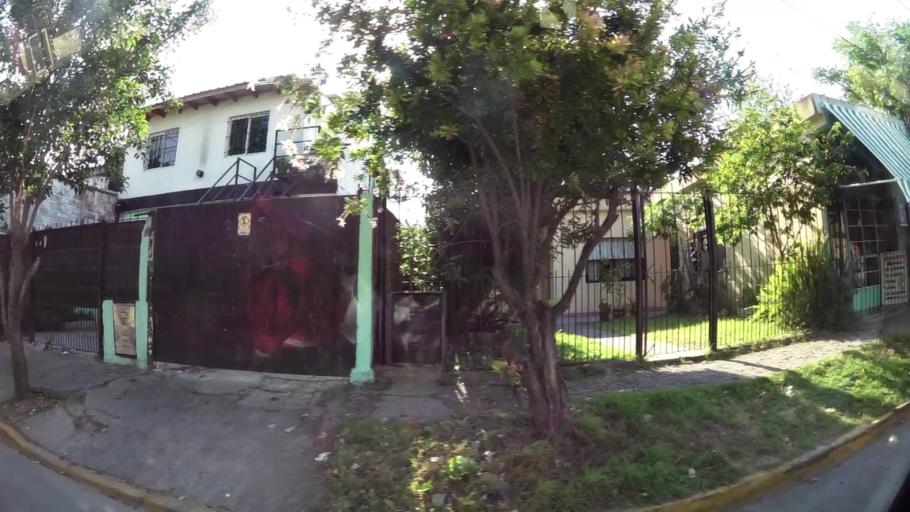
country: AR
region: Buenos Aires
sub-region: Partido de Merlo
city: Merlo
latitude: -34.6600
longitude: -58.7238
